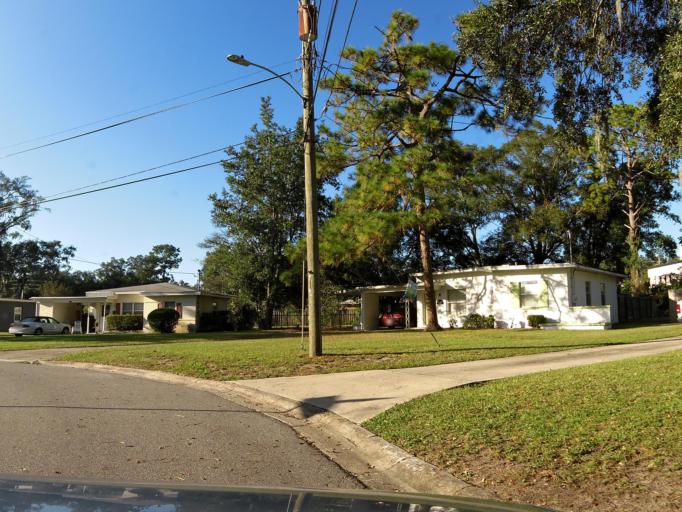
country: US
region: Florida
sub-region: Duval County
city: Jacksonville
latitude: 30.2600
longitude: -81.6385
